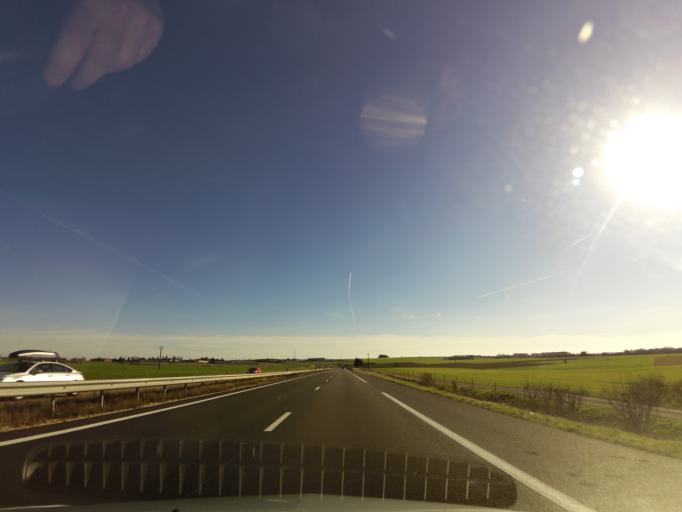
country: FR
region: Bourgogne
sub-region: Departement de l'Yonne
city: Joux-la-Ville
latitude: 47.6707
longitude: 3.8664
